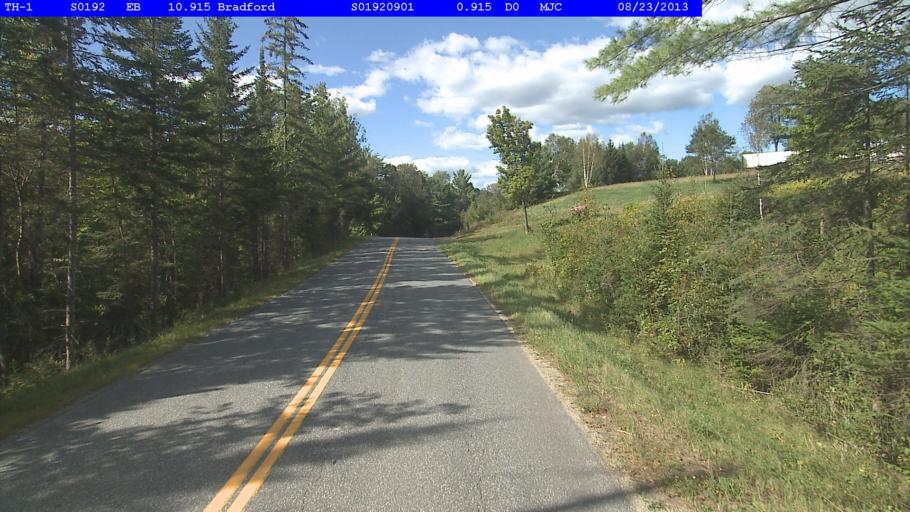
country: US
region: New Hampshire
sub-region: Grafton County
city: Orford
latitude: 44.0216
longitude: -72.2024
